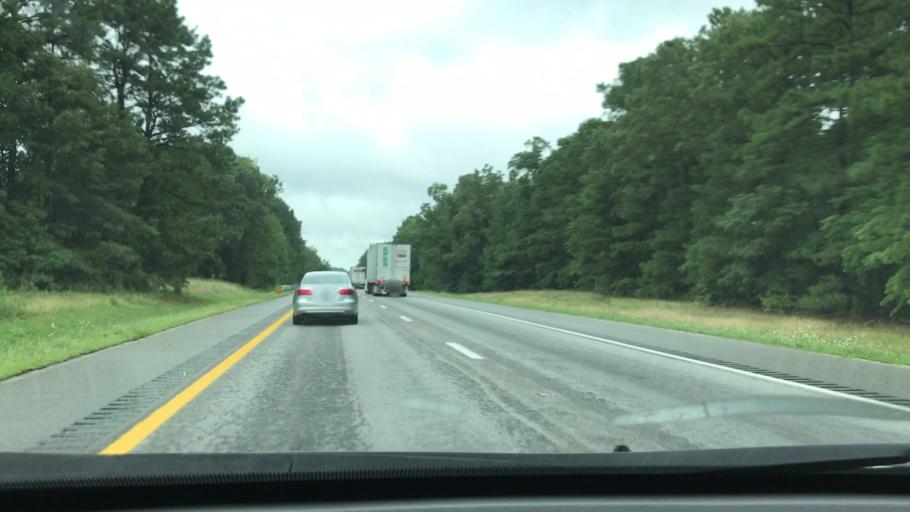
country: US
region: Virginia
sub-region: City of Emporia
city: Emporia
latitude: 36.7805
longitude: -77.4619
